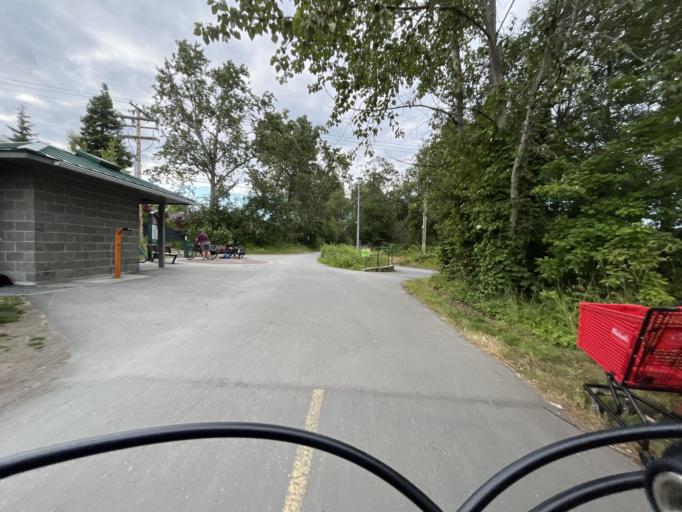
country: CA
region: British Columbia
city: Victoria
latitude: 48.4758
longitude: -123.3596
